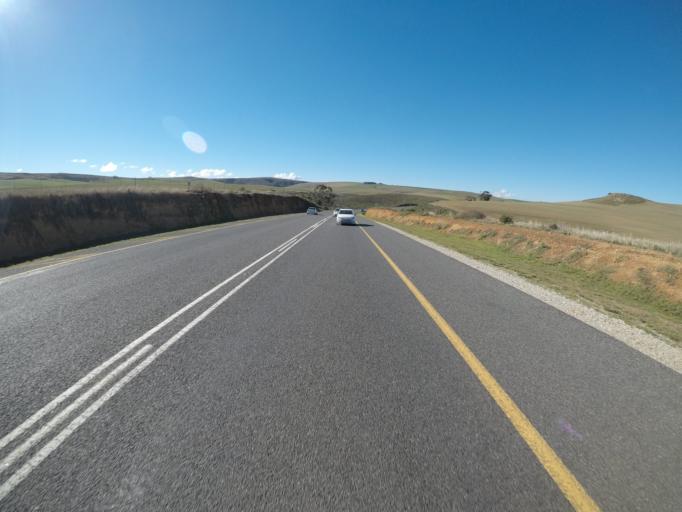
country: ZA
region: Western Cape
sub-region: Overberg District Municipality
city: Hermanus
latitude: -34.2331
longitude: 19.2362
